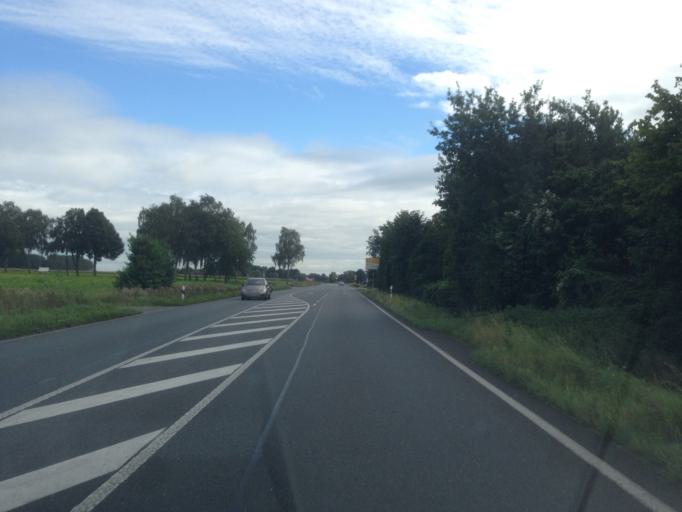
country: DE
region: North Rhine-Westphalia
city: Olfen
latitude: 51.7819
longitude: 7.3574
